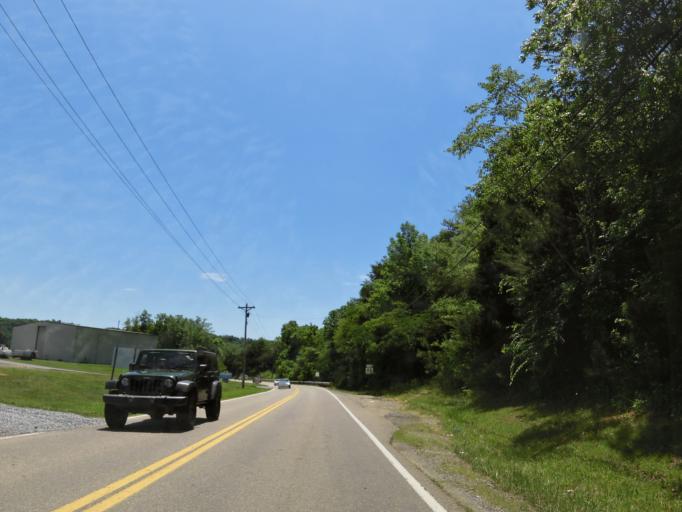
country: US
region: Tennessee
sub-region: Jefferson County
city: Dandridge
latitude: 36.0099
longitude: -83.4113
